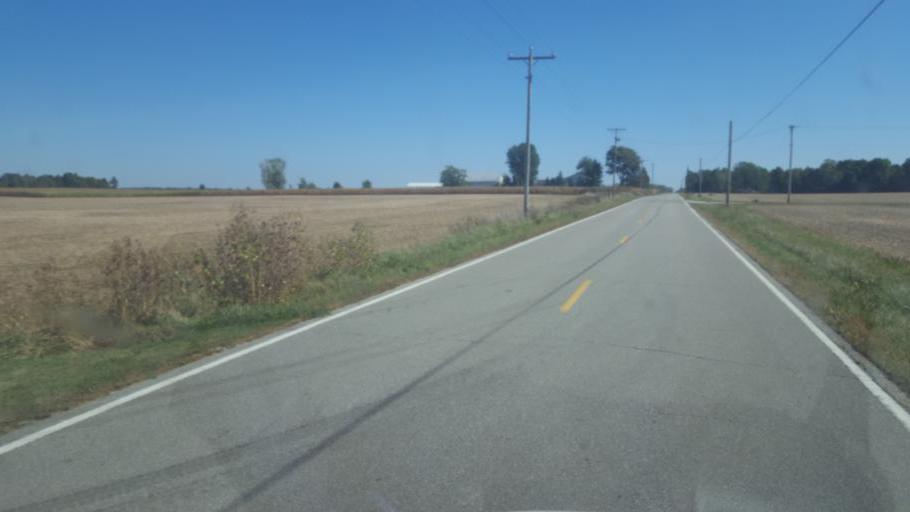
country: US
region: Ohio
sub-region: Crawford County
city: Bucyrus
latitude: 40.8630
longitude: -83.0847
